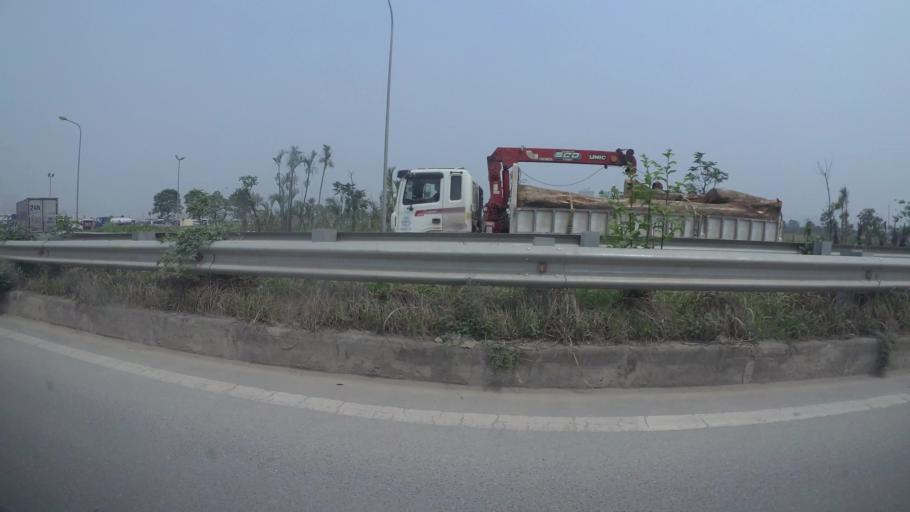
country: VN
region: Ha Noi
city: Cau Dien
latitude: 21.0067
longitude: 105.7494
